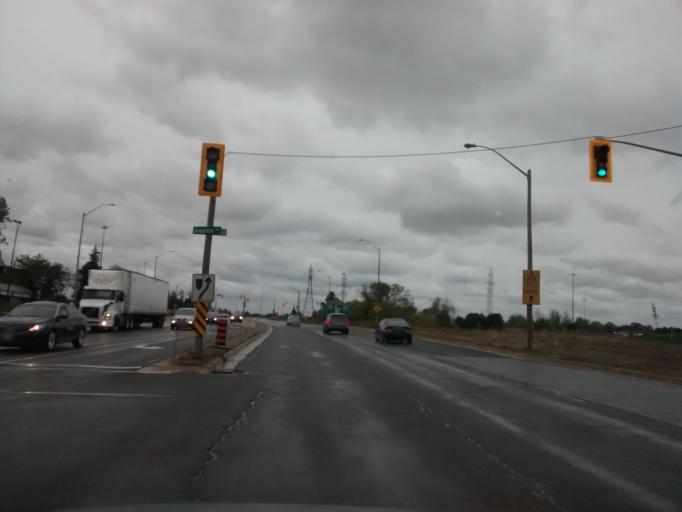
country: CA
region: Ontario
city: Hamilton
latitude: 43.2427
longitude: -79.7580
